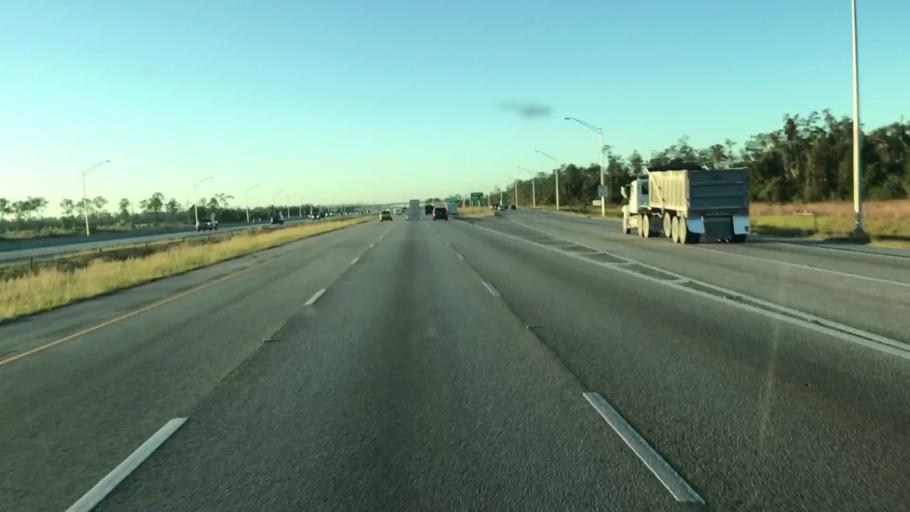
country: US
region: Florida
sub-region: Lee County
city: Three Oaks
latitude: 26.5239
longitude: -81.7954
